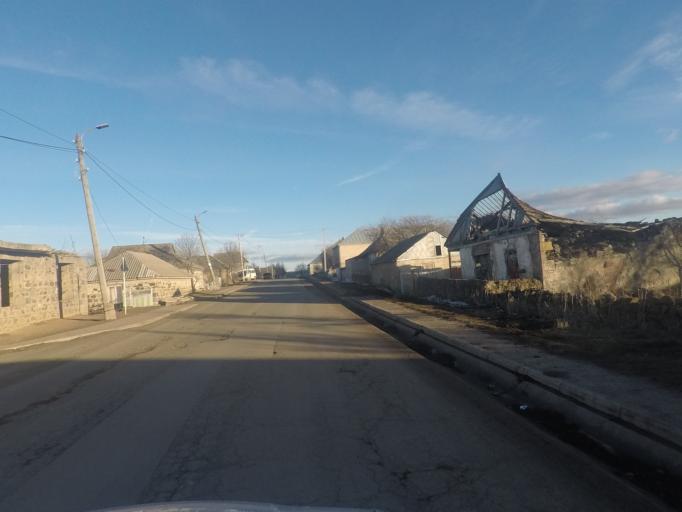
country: GE
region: Kvemo Kartli
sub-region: Tsalka
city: Tsalka
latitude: 41.6039
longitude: 44.0473
